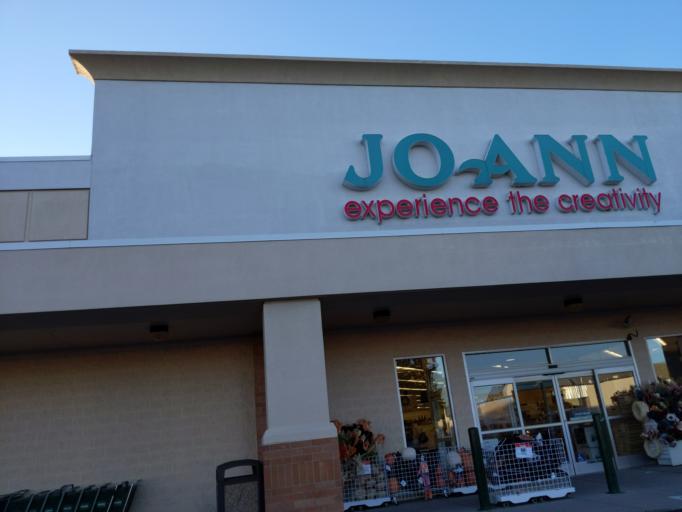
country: US
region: Michigan
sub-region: Ingham County
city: East Lansing
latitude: 42.7394
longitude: -84.5071
